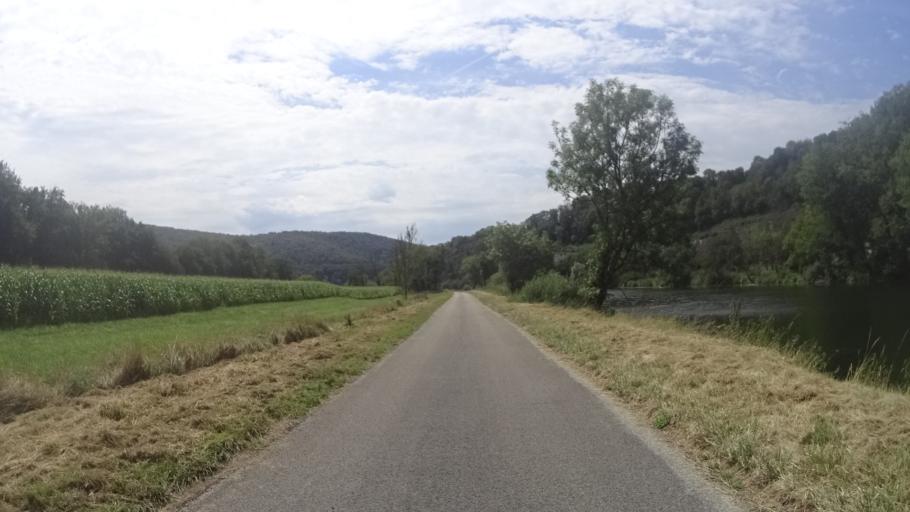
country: FR
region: Franche-Comte
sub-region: Departement du Doubs
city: Clerval
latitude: 47.3718
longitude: 6.4554
